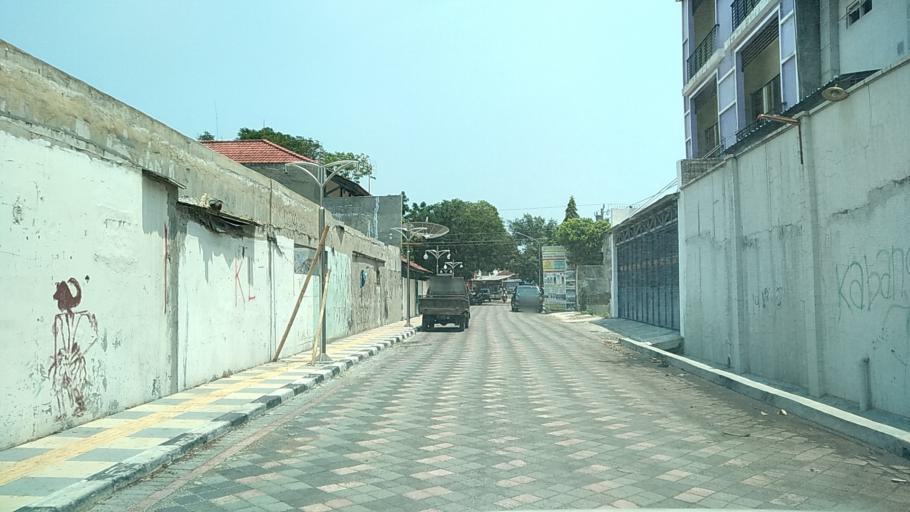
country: ID
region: Central Java
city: Semarang
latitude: -6.9697
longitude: 110.4359
